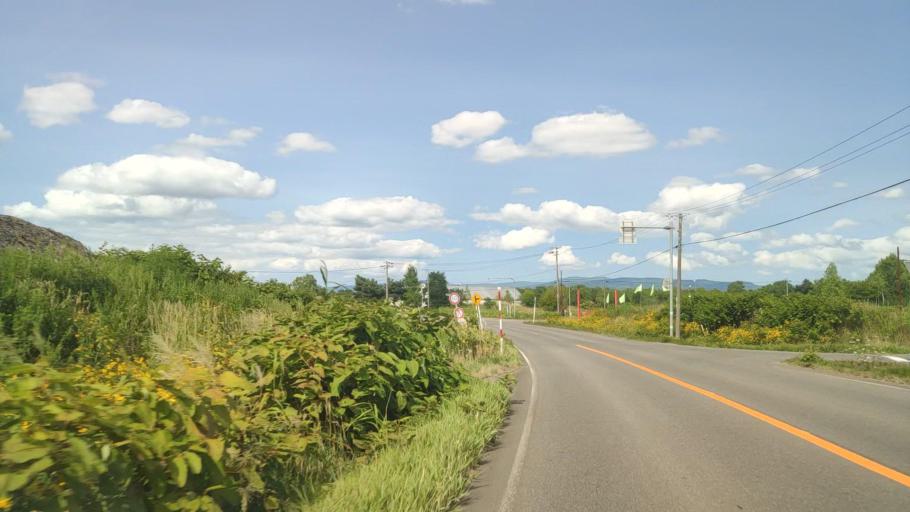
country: JP
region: Hokkaido
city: Nayoro
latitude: 44.2829
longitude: 142.4289
